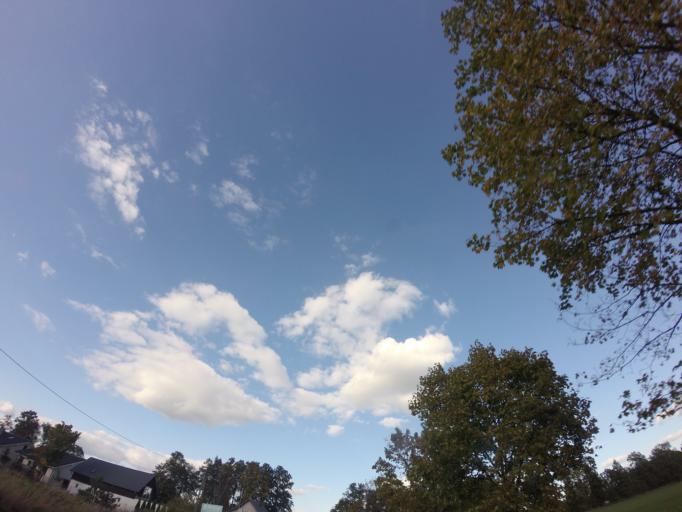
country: PL
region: Greater Poland Voivodeship
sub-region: Powiat nowotomyski
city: Nowy Tomysl
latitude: 52.2591
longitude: 16.1362
